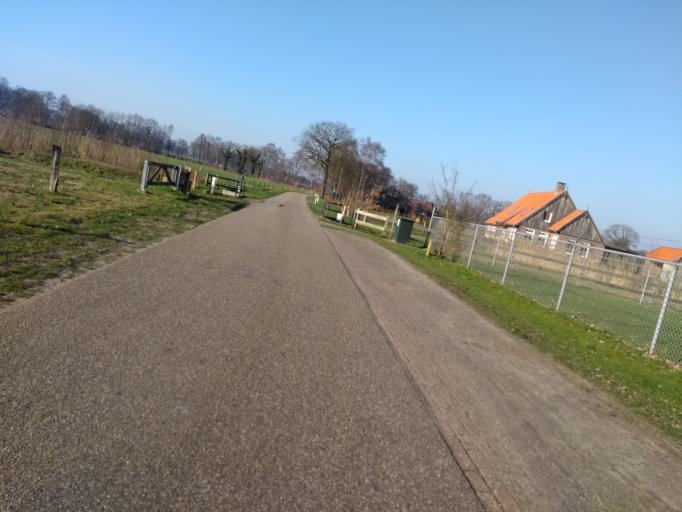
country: NL
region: Overijssel
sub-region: Gemeente Tubbergen
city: Tubbergen
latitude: 52.4098
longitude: 6.7648
